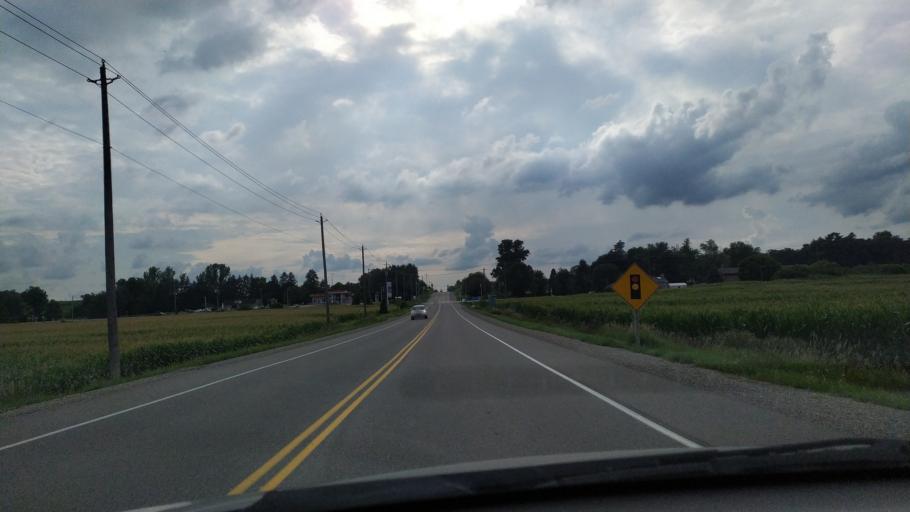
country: CA
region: Ontario
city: Kitchener
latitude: 43.3586
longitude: -80.4783
